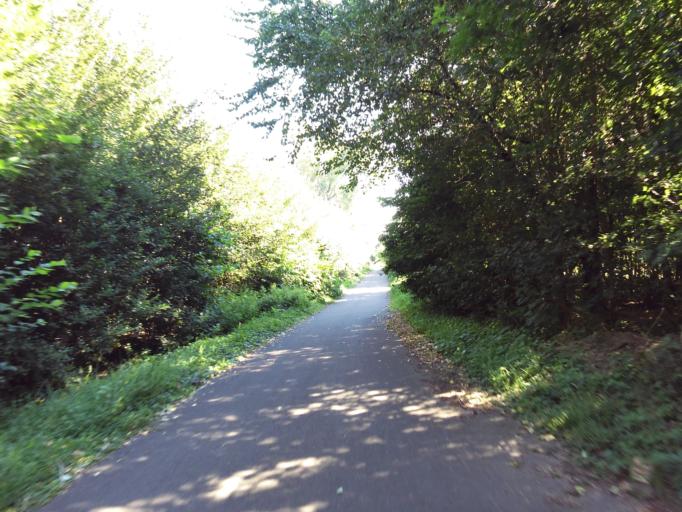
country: DE
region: Rheinland-Pfalz
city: Osthofen
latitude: 49.6799
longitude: 8.3528
